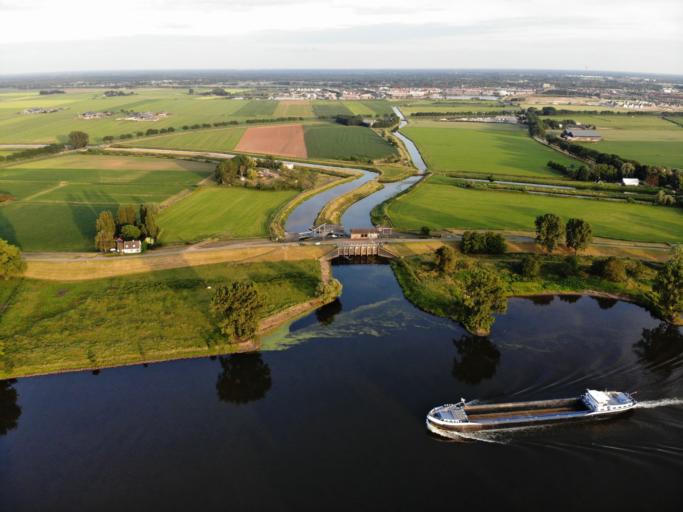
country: NL
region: Gelderland
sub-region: Gemeente Maasdriel
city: Heerewaarden
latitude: 51.7541
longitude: 5.3556
